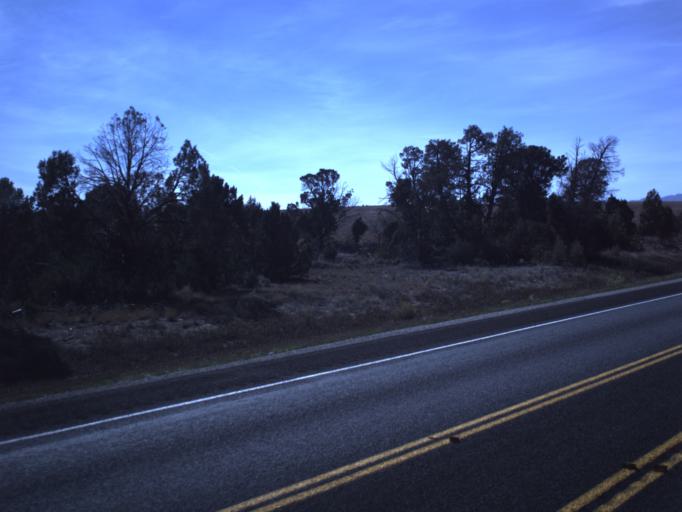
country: US
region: Colorado
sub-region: Dolores County
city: Dove Creek
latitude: 37.8235
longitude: -109.0664
